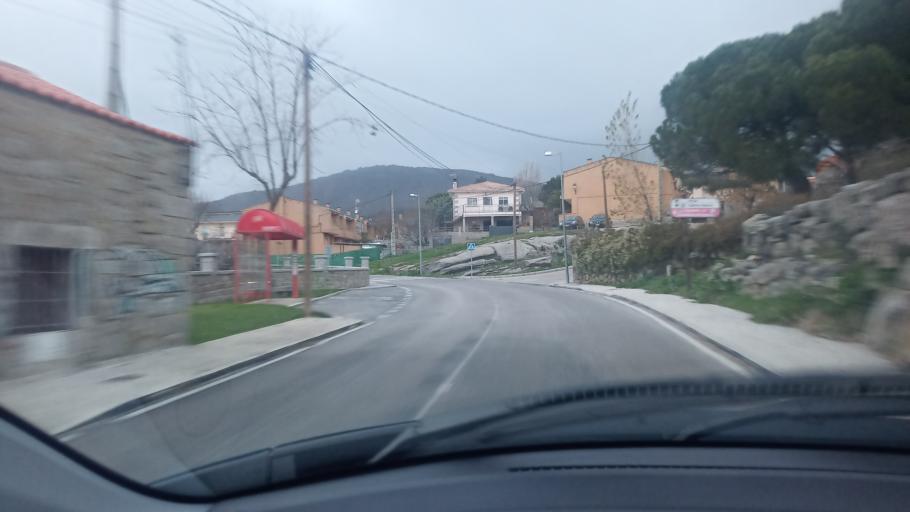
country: ES
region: Madrid
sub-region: Provincia de Madrid
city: Zarzalejo
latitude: 40.5479
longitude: -4.1791
